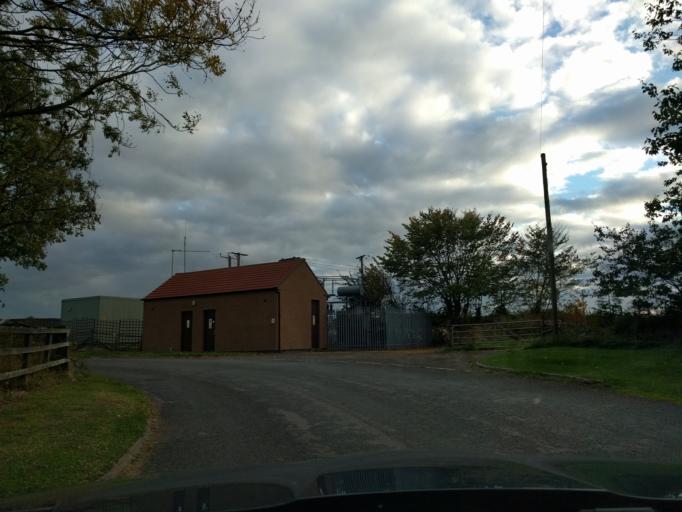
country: GB
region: England
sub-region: Northumberland
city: Ford
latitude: 55.7416
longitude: -2.1105
